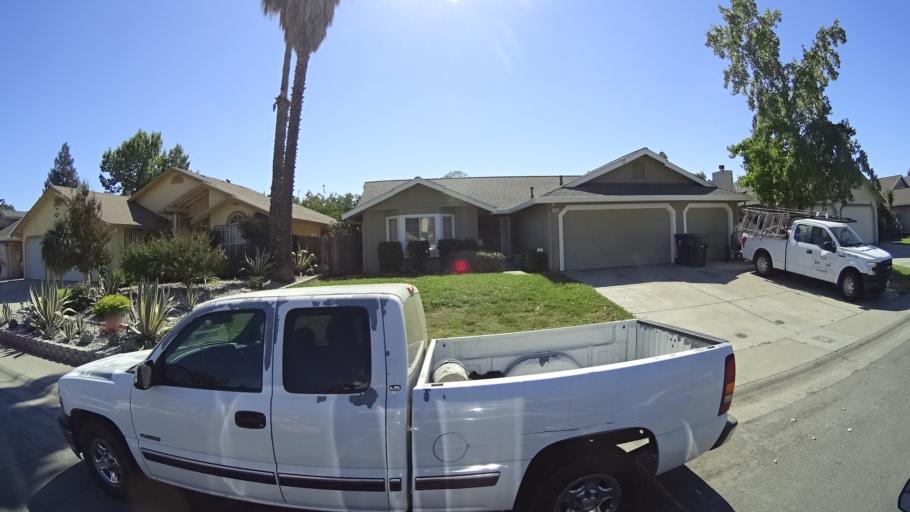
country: US
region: California
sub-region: Sacramento County
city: Parkway
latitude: 38.4728
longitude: -121.4407
